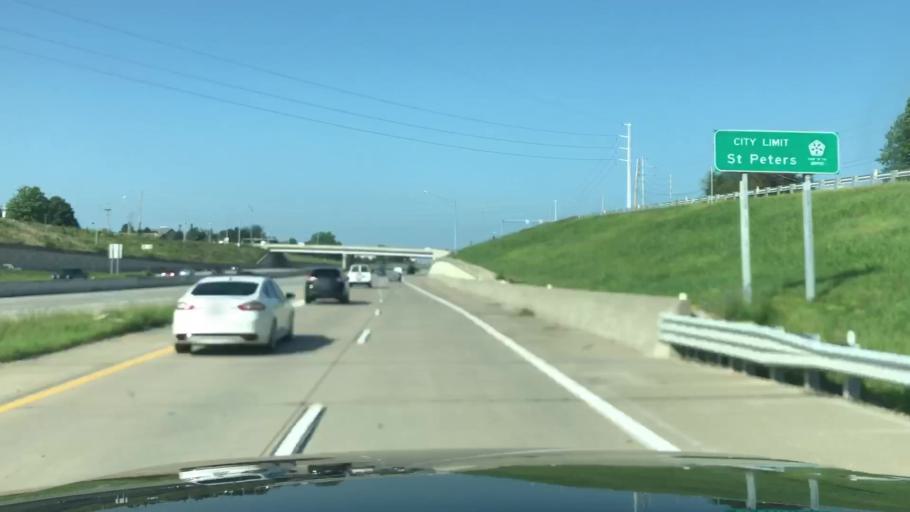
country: US
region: Missouri
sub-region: Saint Charles County
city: Saint Charles
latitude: 38.7541
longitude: -90.5508
